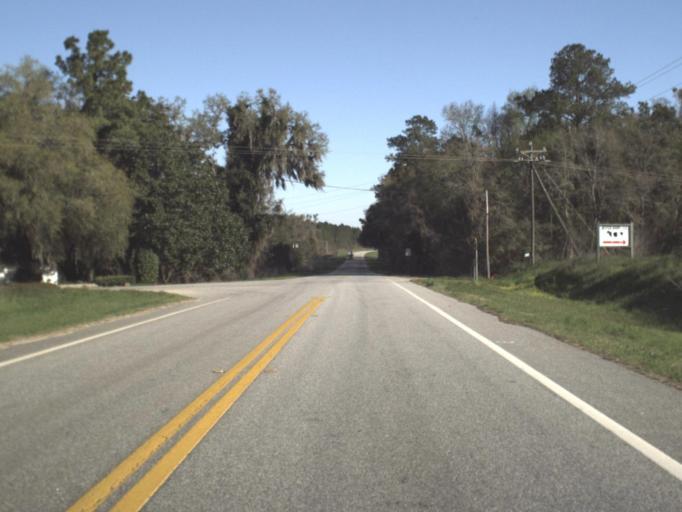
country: US
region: Georgia
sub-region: Brooks County
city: Quitman
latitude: 30.6161
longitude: -83.6466
